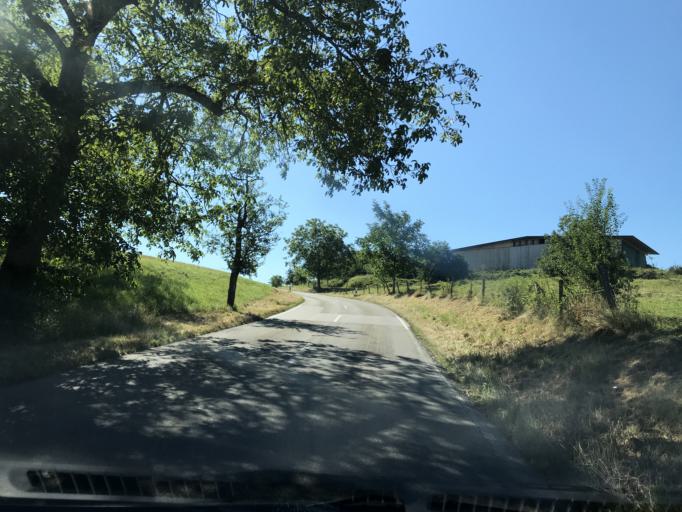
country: DE
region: Baden-Wuerttemberg
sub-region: Freiburg Region
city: Schopfheim
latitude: 47.6304
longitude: 7.8163
